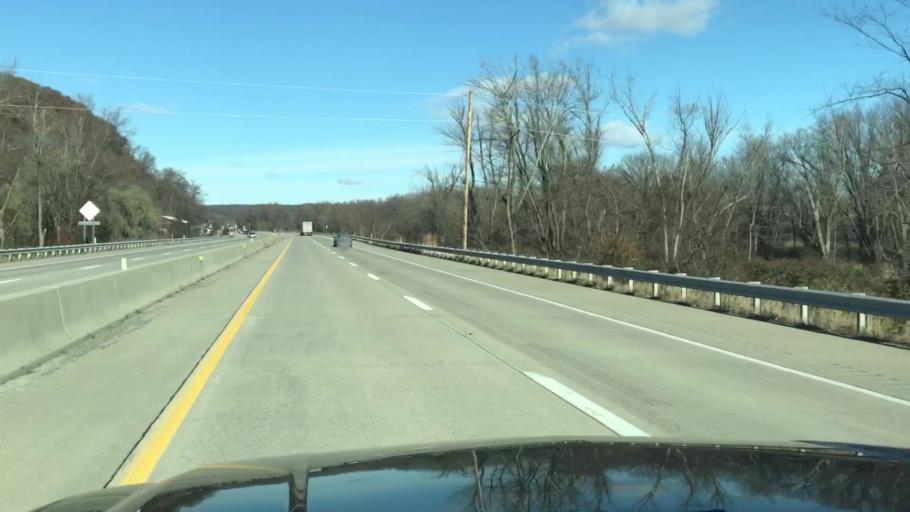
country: US
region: Pennsylvania
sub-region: Dauphin County
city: Millersburg
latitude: 40.5530
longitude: -76.9899
